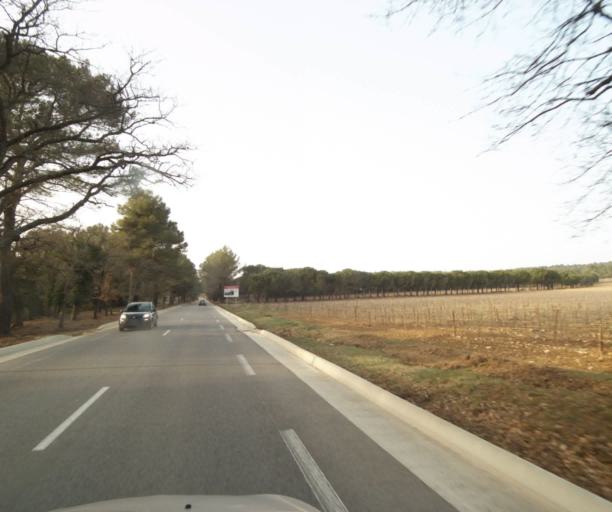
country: FR
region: Provence-Alpes-Cote d'Azur
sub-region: Departement des Bouches-du-Rhone
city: Eguilles
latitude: 43.6133
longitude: 5.3629
